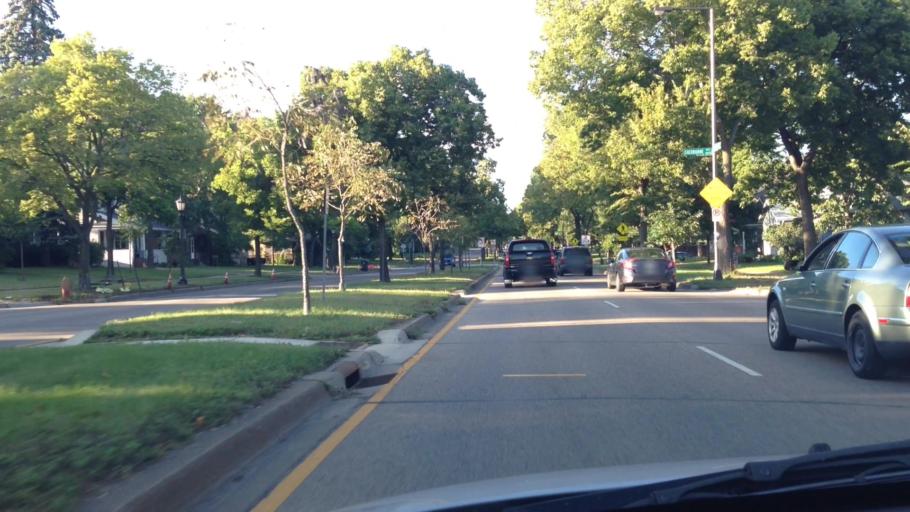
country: US
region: Minnesota
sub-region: Ramsey County
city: Falcon Heights
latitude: 44.9565
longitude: -93.1466
